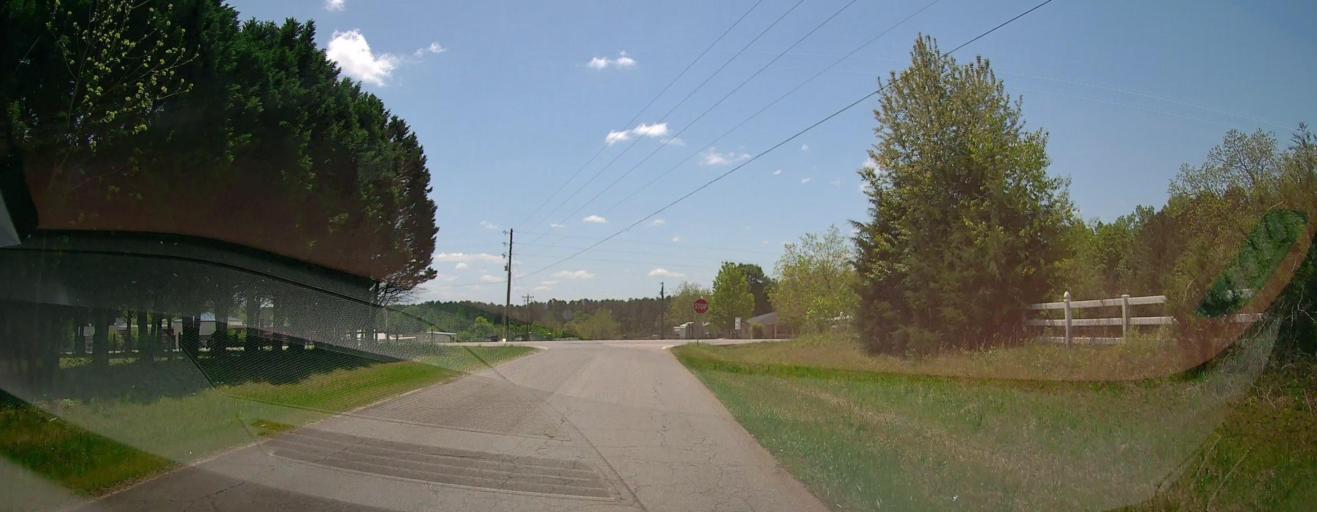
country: US
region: Georgia
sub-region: Jasper County
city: Monticello
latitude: 33.3193
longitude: -83.7161
